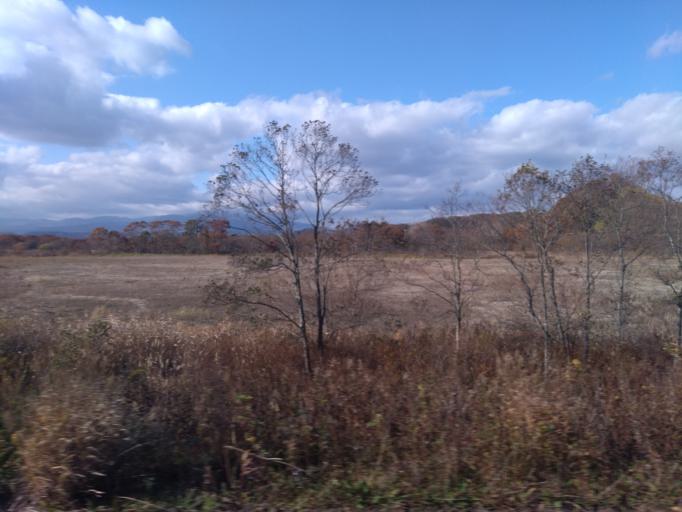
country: JP
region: Hokkaido
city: Shiraoi
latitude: 42.5344
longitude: 141.3268
